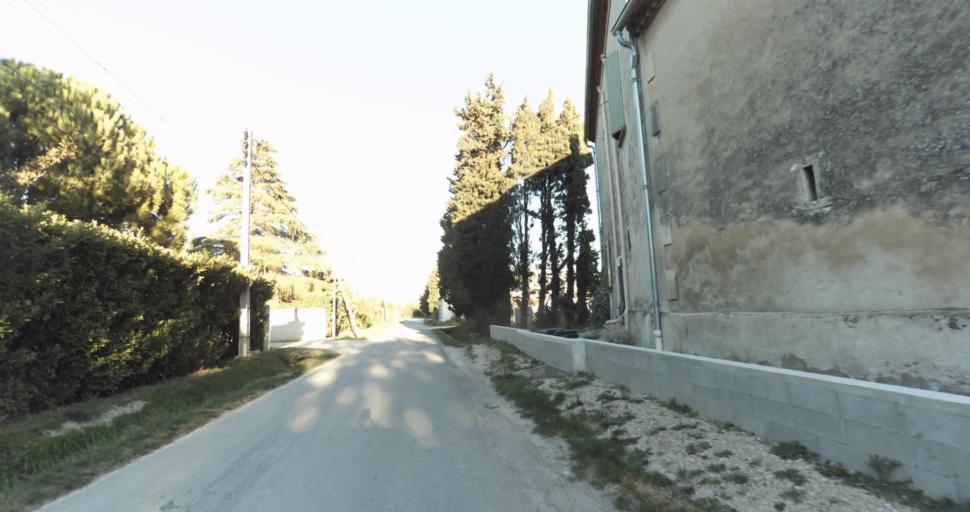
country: FR
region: Provence-Alpes-Cote d'Azur
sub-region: Departement des Bouches-du-Rhone
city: Barbentane
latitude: 43.9065
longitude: 4.7557
